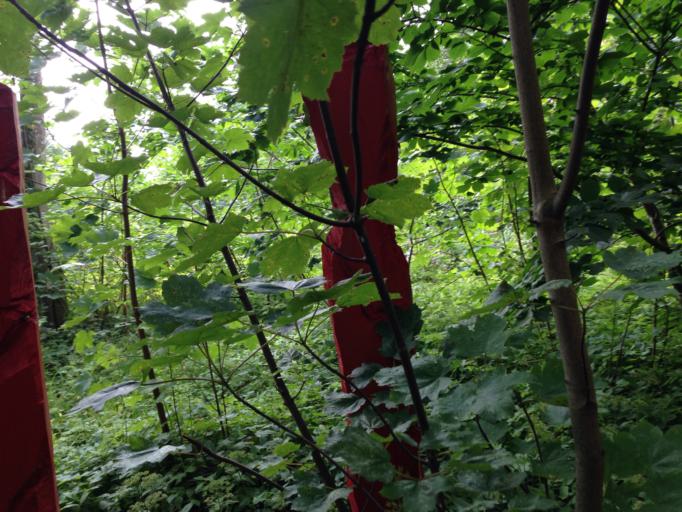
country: SE
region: Skane
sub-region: Ystads Kommun
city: Ystad
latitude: 55.4636
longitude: 13.7120
